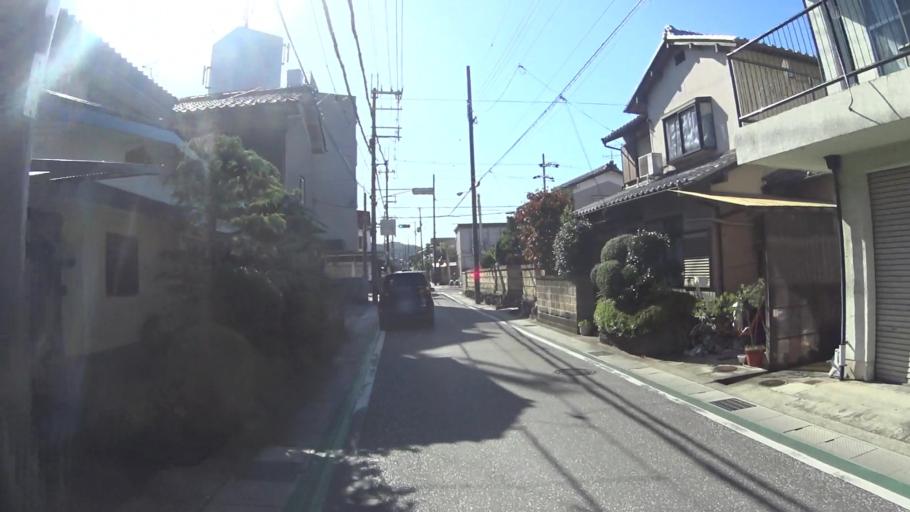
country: JP
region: Kyoto
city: Kameoka
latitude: 35.0104
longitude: 135.5885
